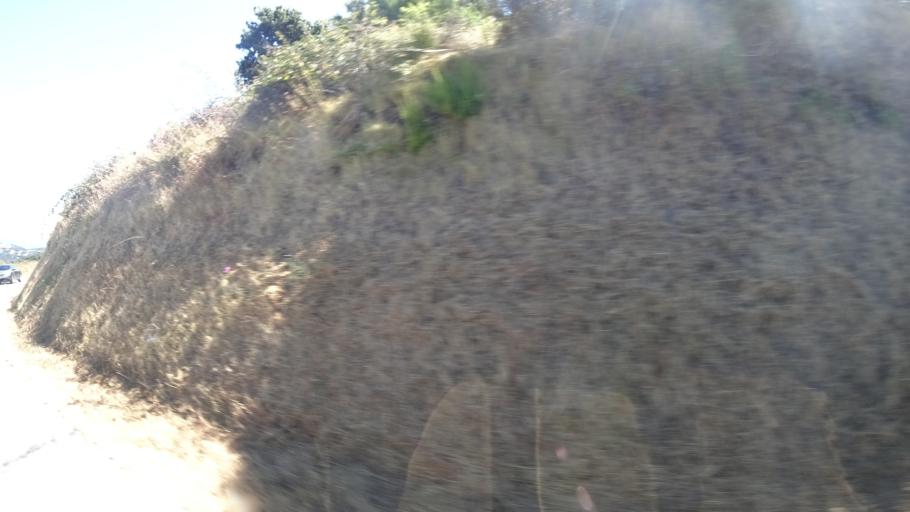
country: FR
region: Corsica
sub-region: Departement de la Corse-du-Sud
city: Alata
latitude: 41.9702
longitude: 8.6982
